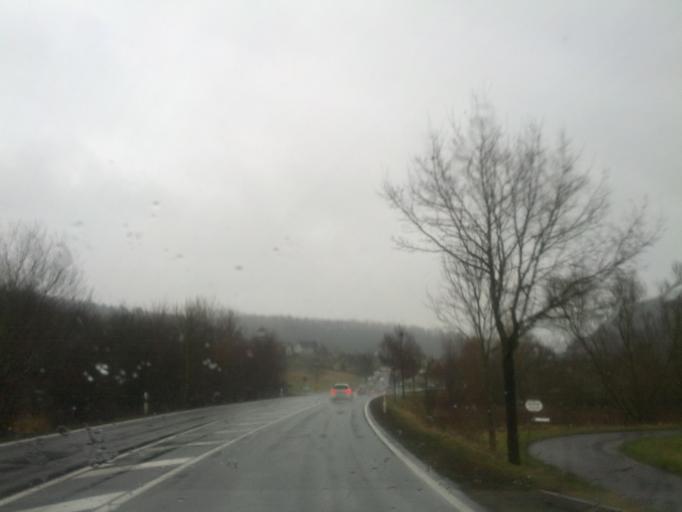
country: DE
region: Hesse
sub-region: Regierungsbezirk Kassel
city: Sontra
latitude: 51.0726
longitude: 9.9937
